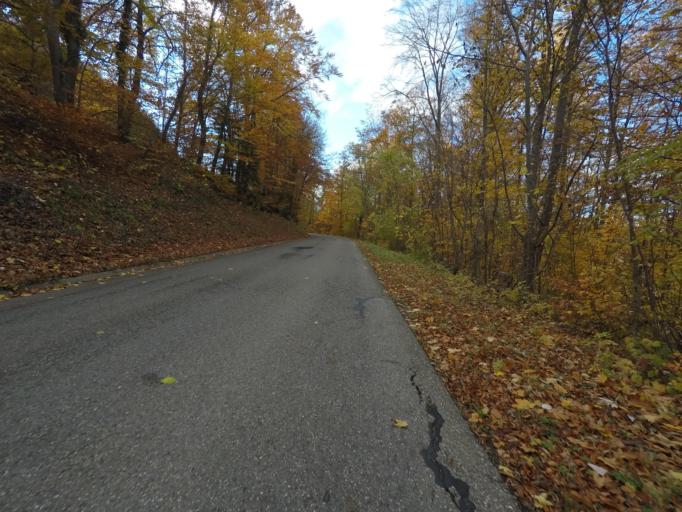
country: DE
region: Baden-Wuerttemberg
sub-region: Tuebingen Region
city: Pfullingen
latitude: 48.4240
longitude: 9.2476
